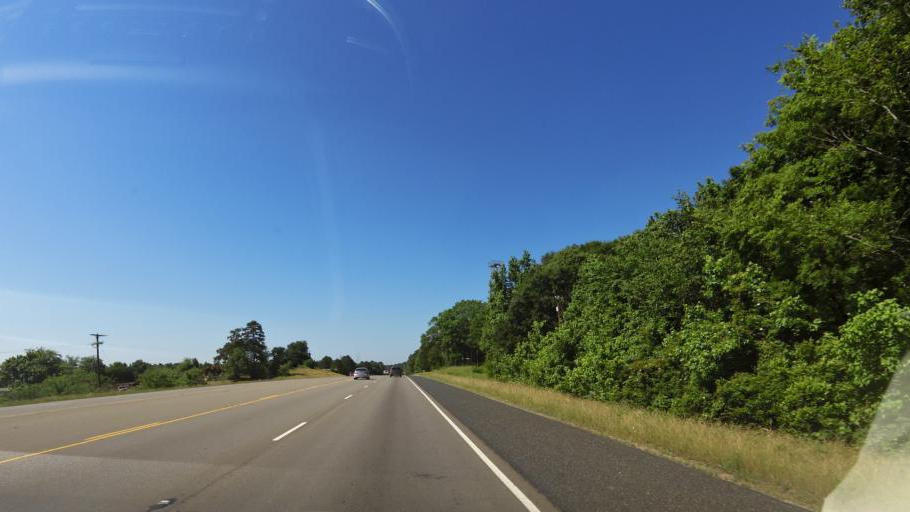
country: US
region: Texas
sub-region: Nacogdoches County
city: Nacogdoches
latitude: 31.5560
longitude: -94.6836
